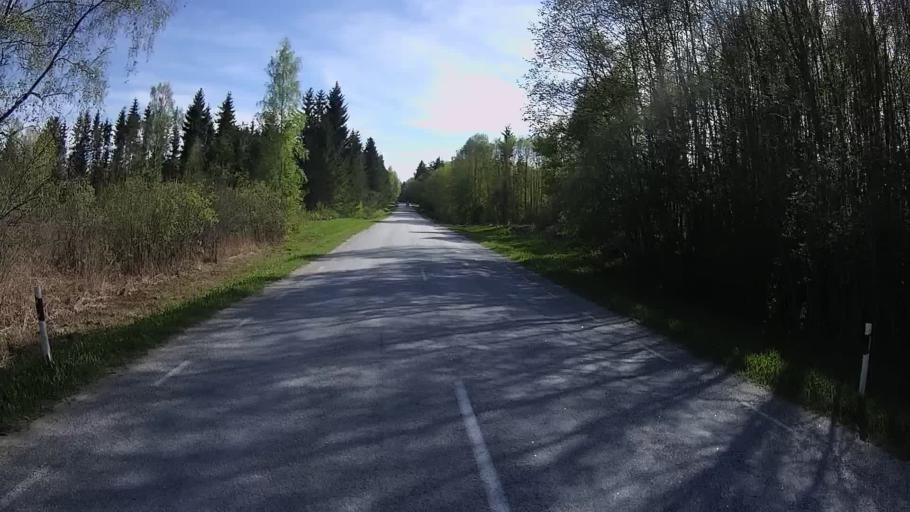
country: EE
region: Vorumaa
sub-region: Antsla vald
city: Vana-Antsla
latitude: 58.0016
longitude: 26.4984
